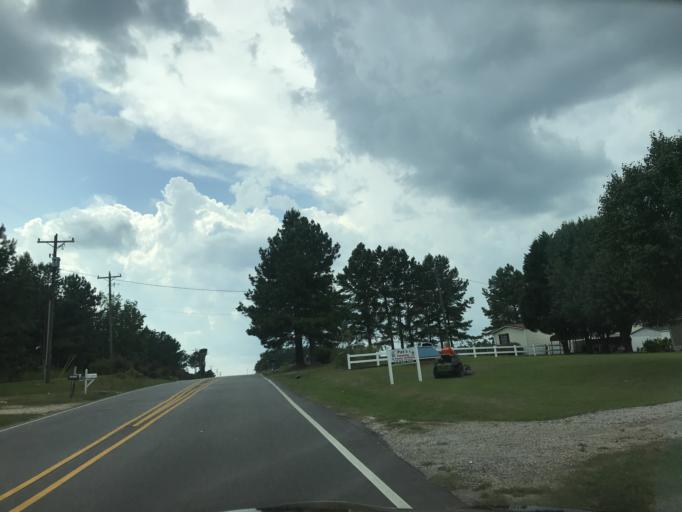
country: US
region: North Carolina
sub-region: Johnston County
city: Four Oaks
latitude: 35.5096
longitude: -78.5228
